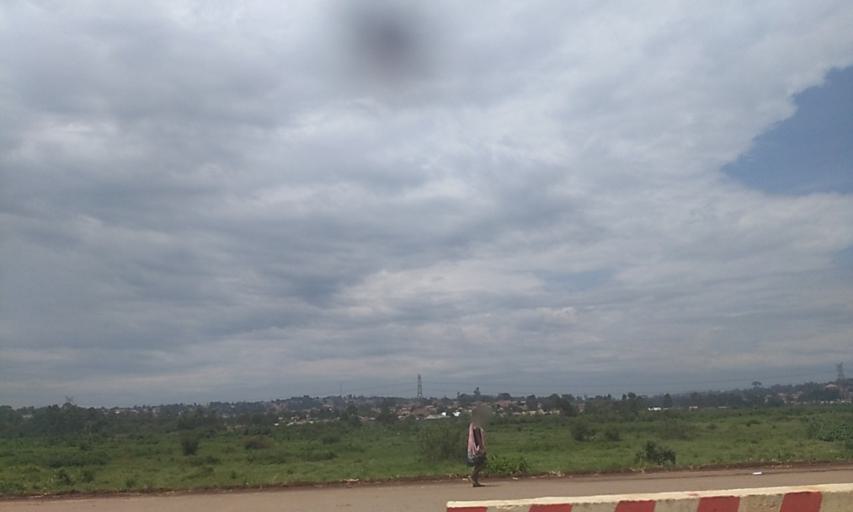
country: UG
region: Central Region
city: Kampala Central Division
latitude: 0.3416
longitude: 32.5351
